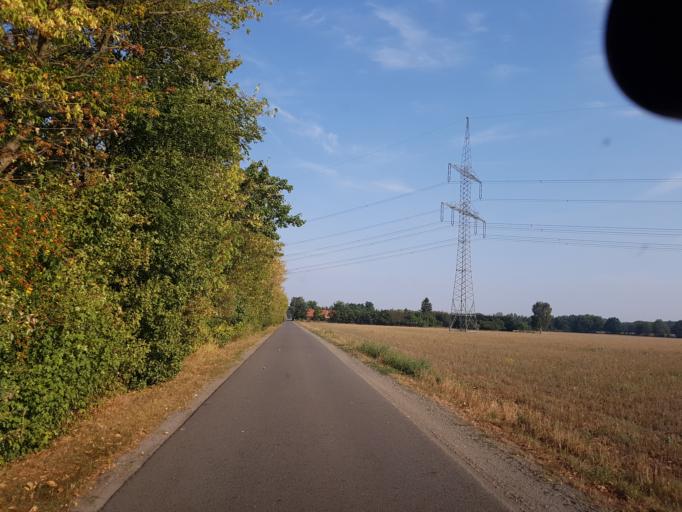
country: DE
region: Brandenburg
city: Finsterwalde
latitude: 51.6534
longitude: 13.7222
